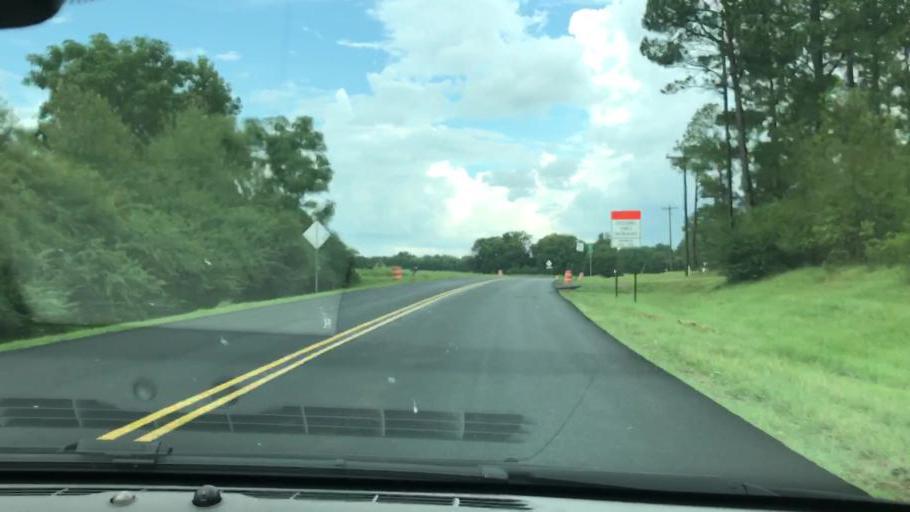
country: US
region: Georgia
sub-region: Early County
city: Blakely
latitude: 31.4024
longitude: -84.9597
